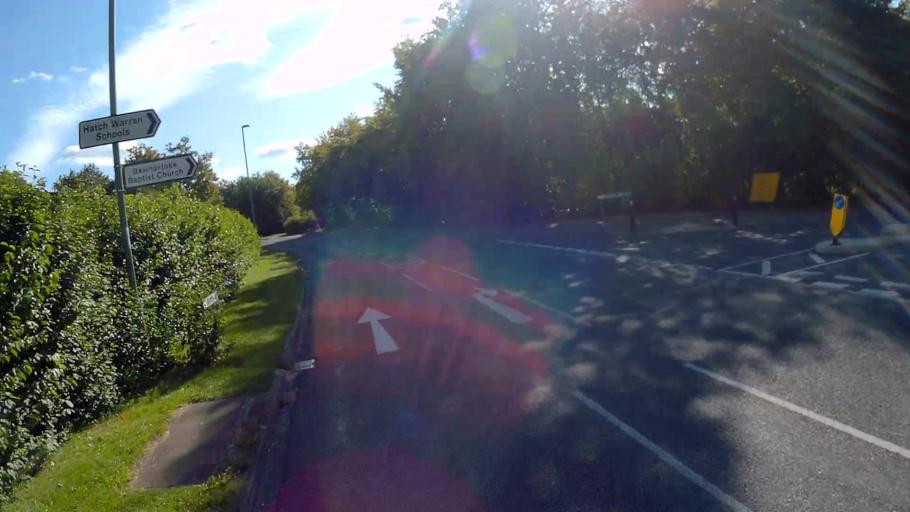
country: GB
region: England
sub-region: Hampshire
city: Basingstoke
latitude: 51.2441
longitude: -1.1172
